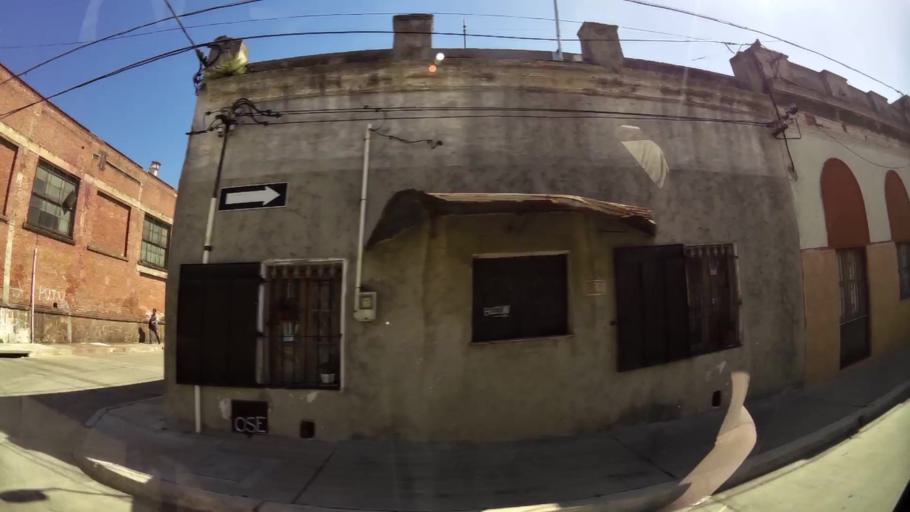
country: UY
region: Montevideo
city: Montevideo
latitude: -34.8492
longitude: -56.2304
